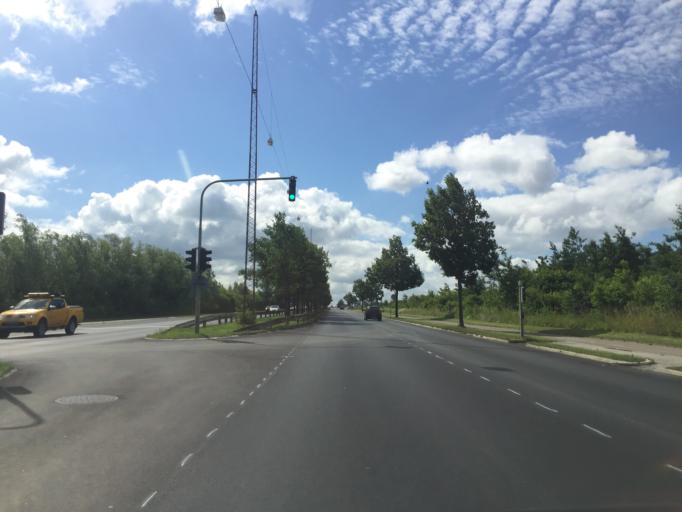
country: DK
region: Capital Region
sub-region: Hvidovre Kommune
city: Hvidovre
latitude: 55.6540
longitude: 12.4557
